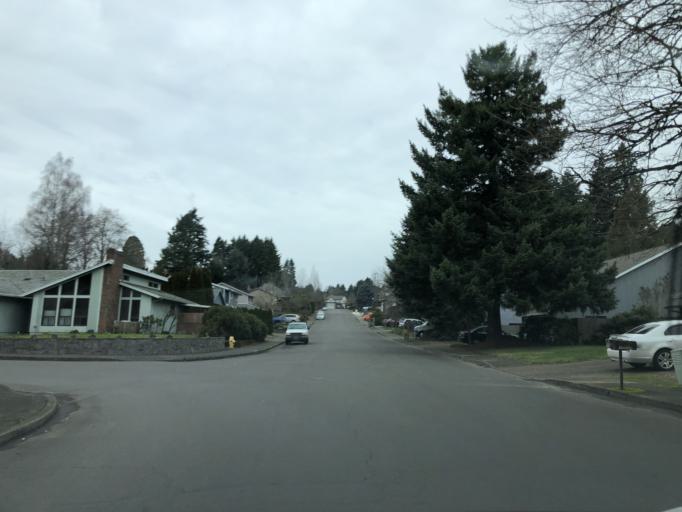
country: US
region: Oregon
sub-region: Washington County
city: Tigard
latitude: 45.4163
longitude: -122.7652
